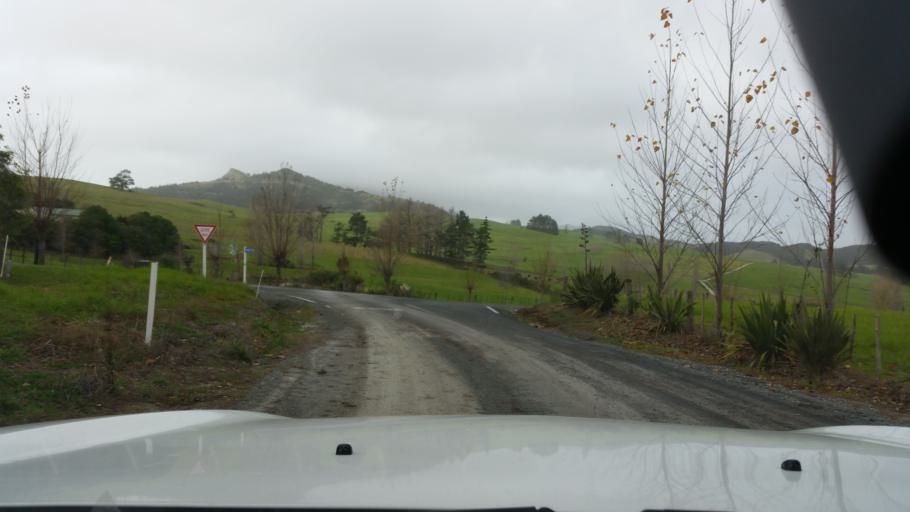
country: NZ
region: Northland
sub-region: Whangarei
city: Ngunguru
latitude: -35.7629
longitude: 174.4946
